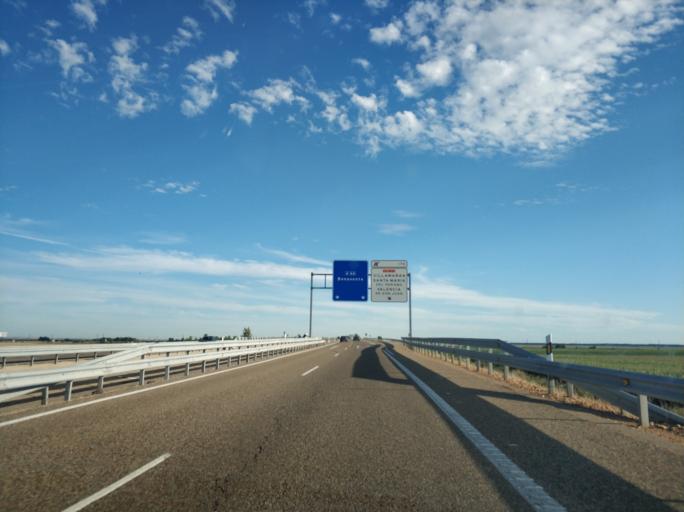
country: ES
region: Castille and Leon
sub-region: Provincia de Leon
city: Villamanan
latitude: 42.3322
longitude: -5.6097
